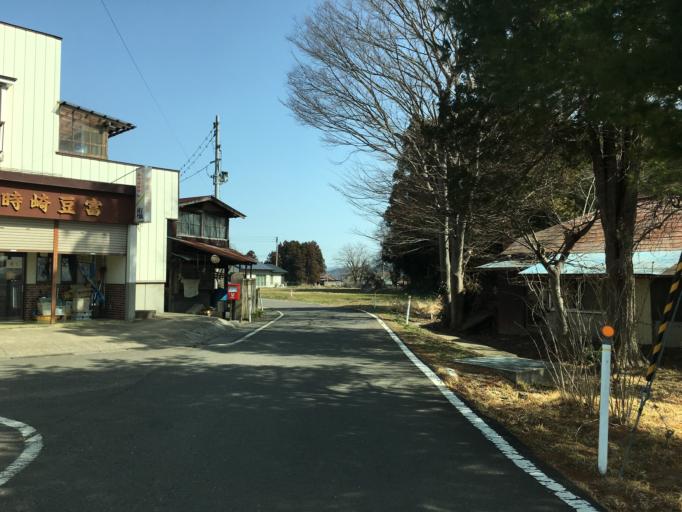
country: JP
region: Fukushima
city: Motomiya
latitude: 37.5346
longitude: 140.3753
